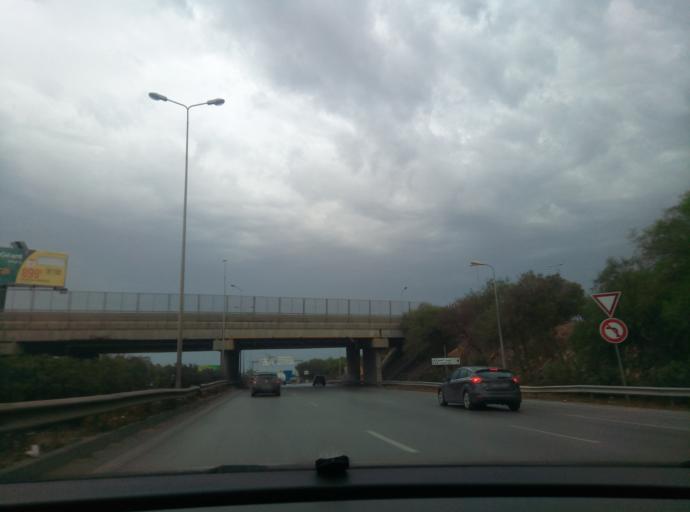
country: TN
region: Bin 'Arus
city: Ben Arous
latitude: 36.7471
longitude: 10.2092
